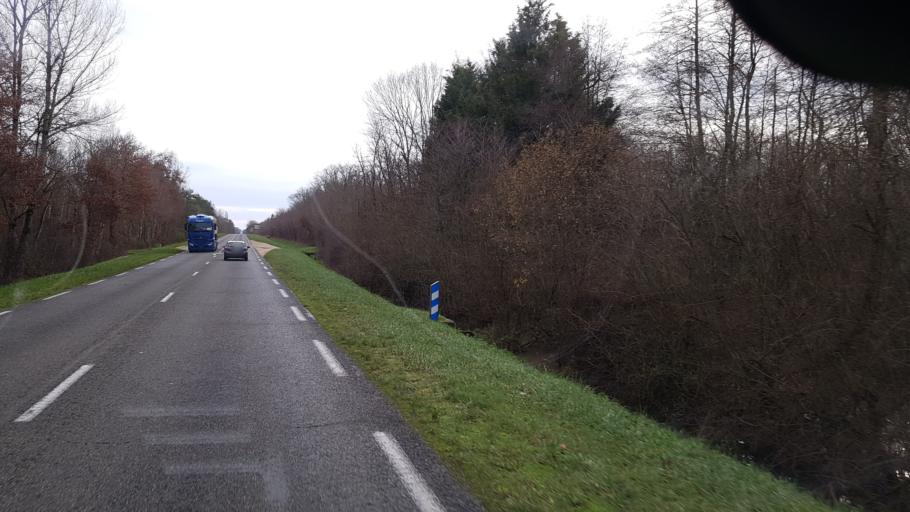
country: FR
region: Centre
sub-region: Departement du Loiret
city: La Ferte-Saint-Aubin
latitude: 47.6940
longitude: 1.9541
